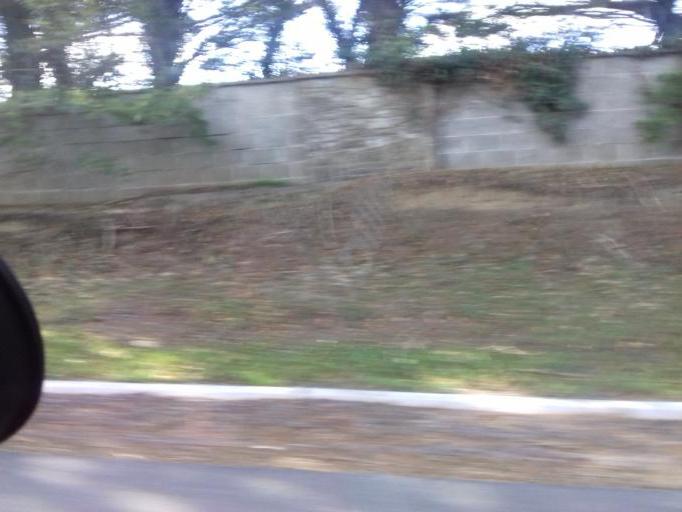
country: IE
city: Kentstown
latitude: 53.6194
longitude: -6.4835
